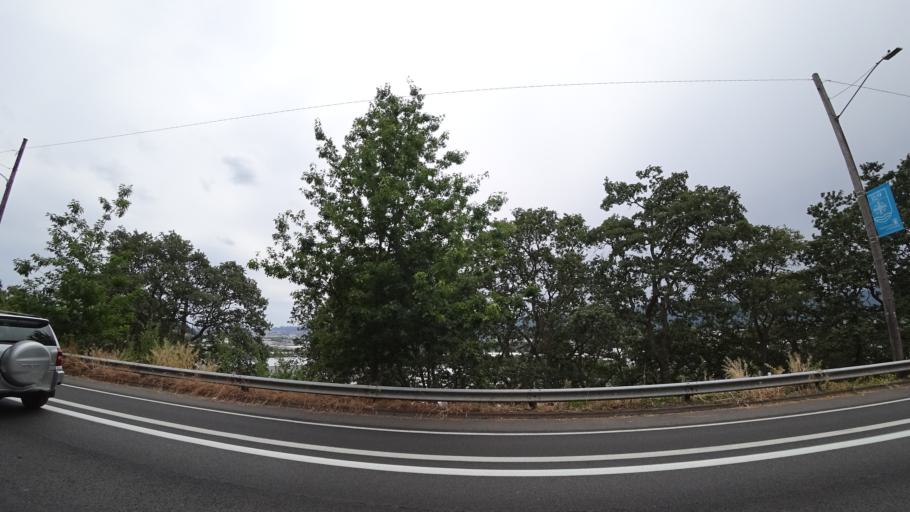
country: US
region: Oregon
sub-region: Multnomah County
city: Portland
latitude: 45.5746
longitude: -122.7064
